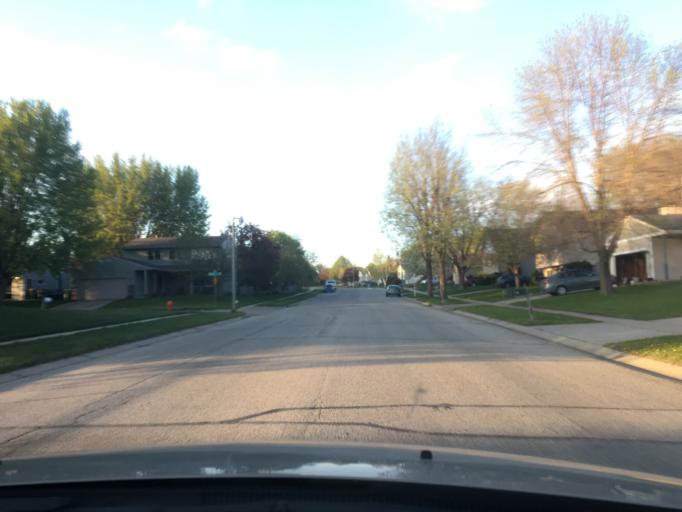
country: US
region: Minnesota
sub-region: Olmsted County
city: Rochester
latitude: 44.0822
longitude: -92.5282
